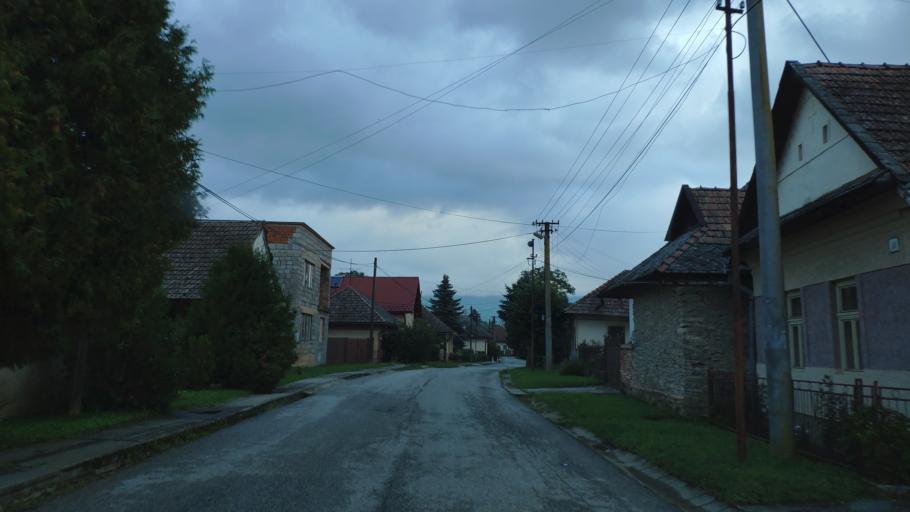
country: SK
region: Kosicky
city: Moldava nad Bodvou
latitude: 48.5796
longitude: 20.8873
